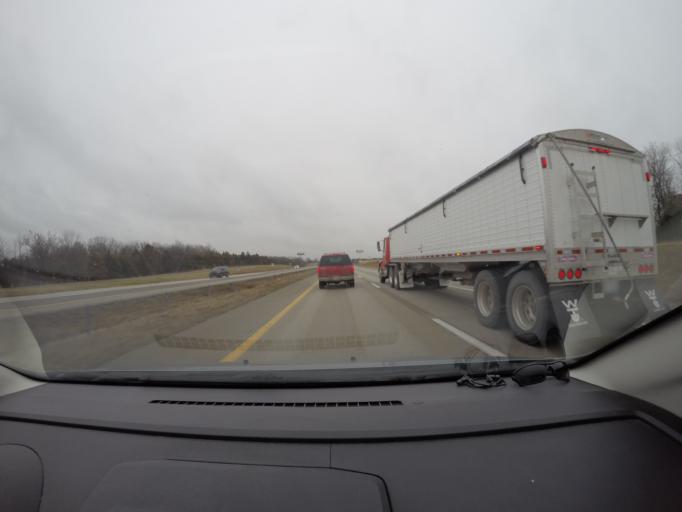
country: US
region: Missouri
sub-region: Callaway County
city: Fulton
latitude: 38.9311
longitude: -91.7962
